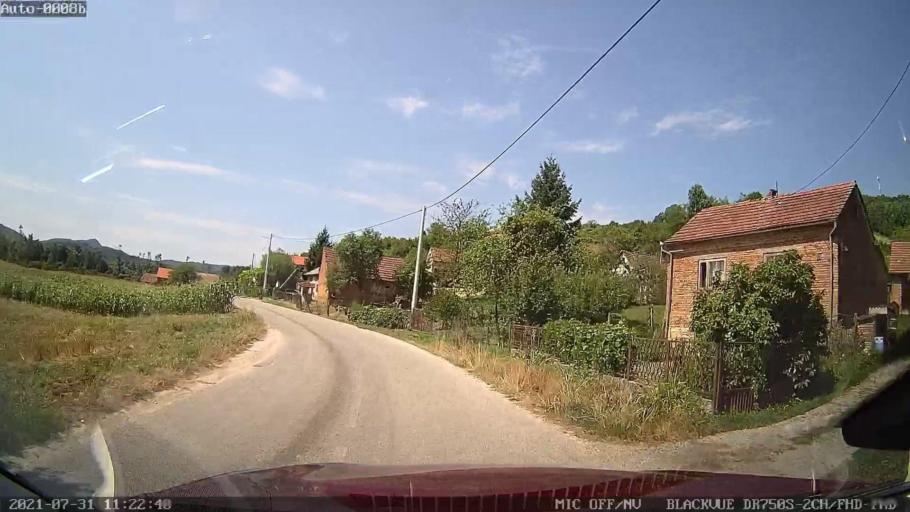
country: HR
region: Varazdinska
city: Jalzabet
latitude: 46.2210
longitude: 16.4669
